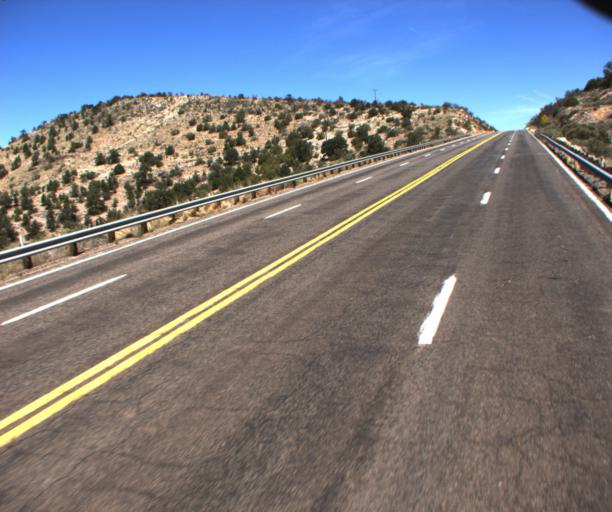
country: US
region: Arizona
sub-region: Mohave County
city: Peach Springs
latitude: 35.5455
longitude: -113.4001
